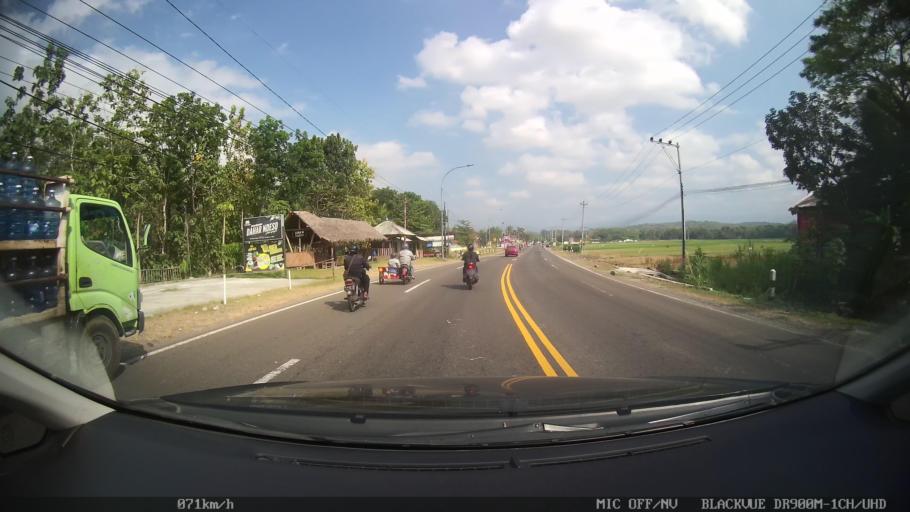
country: ID
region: Daerah Istimewa Yogyakarta
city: Srandakan
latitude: -7.8724
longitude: 110.1982
